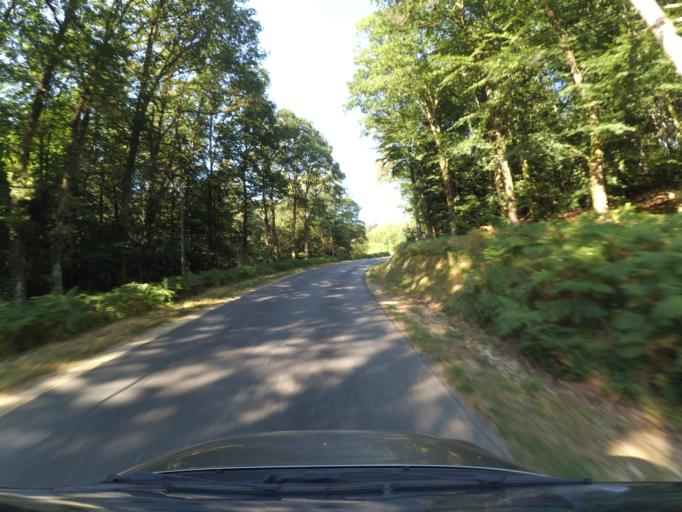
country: FR
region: Limousin
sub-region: Departement de la Haute-Vienne
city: Peyrat-le-Chateau
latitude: 45.7669
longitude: 1.8246
